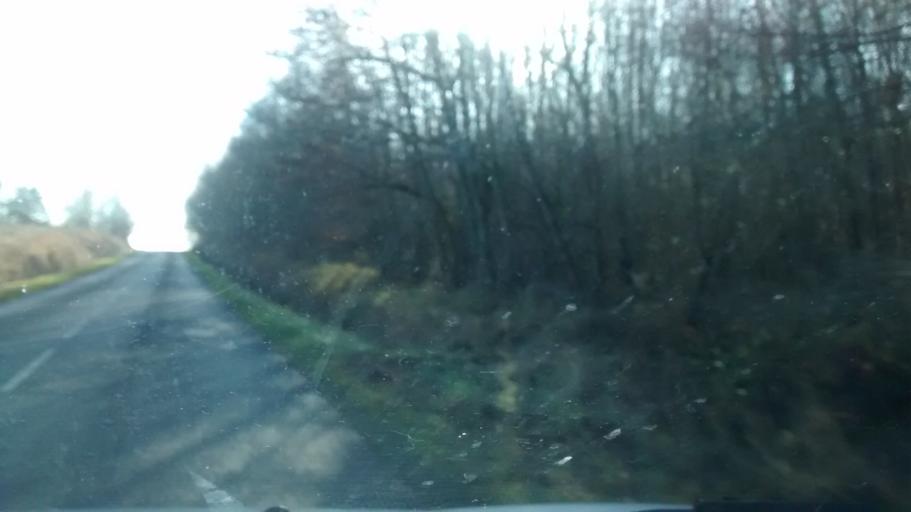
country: FR
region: Centre
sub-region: Departement d'Indre-et-Loire
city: Nazelles-Negron
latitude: 47.4520
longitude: 0.9469
